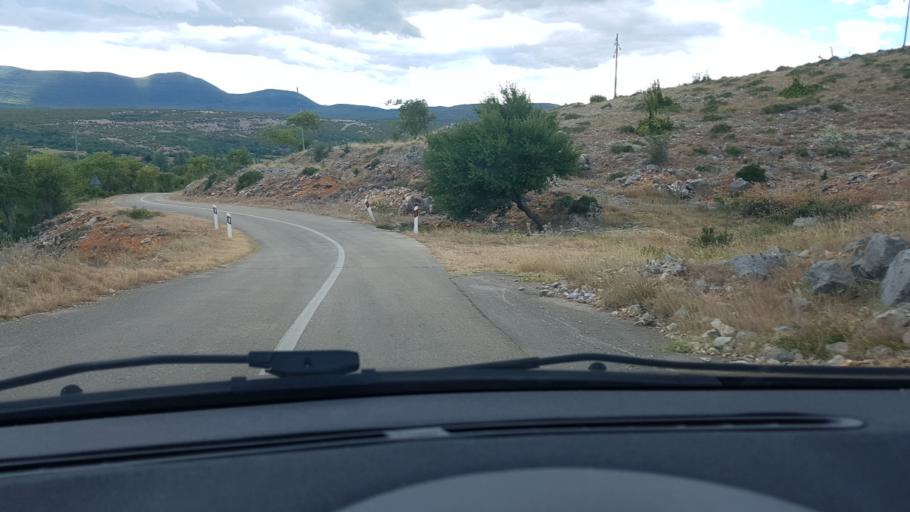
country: HR
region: Zadarska
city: Gracac
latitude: 44.1640
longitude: 15.8661
